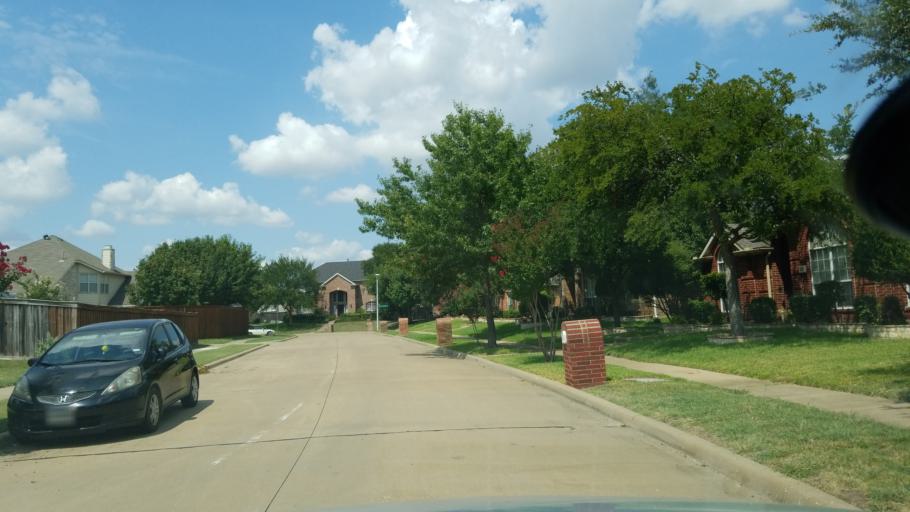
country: US
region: Texas
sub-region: Dallas County
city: Garland
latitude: 32.9226
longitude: -96.6587
